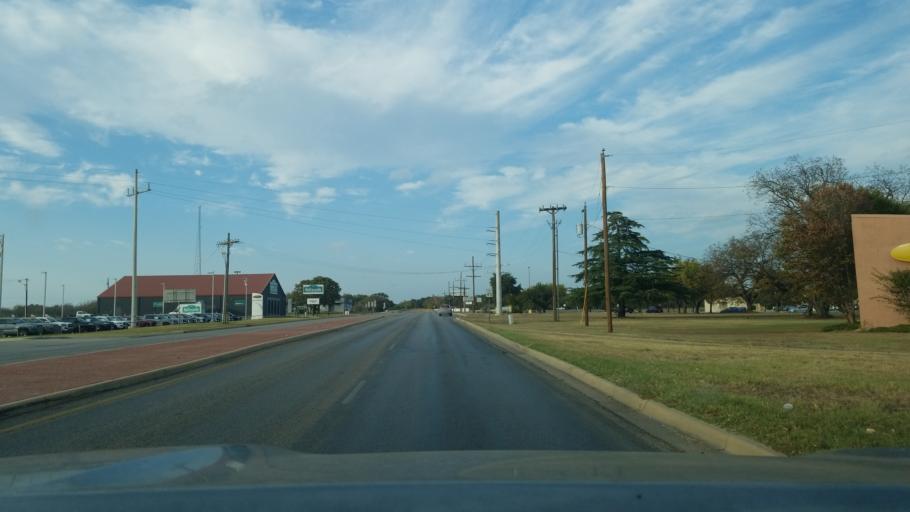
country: US
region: Texas
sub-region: Brown County
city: Early
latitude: 31.7361
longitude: -98.9631
